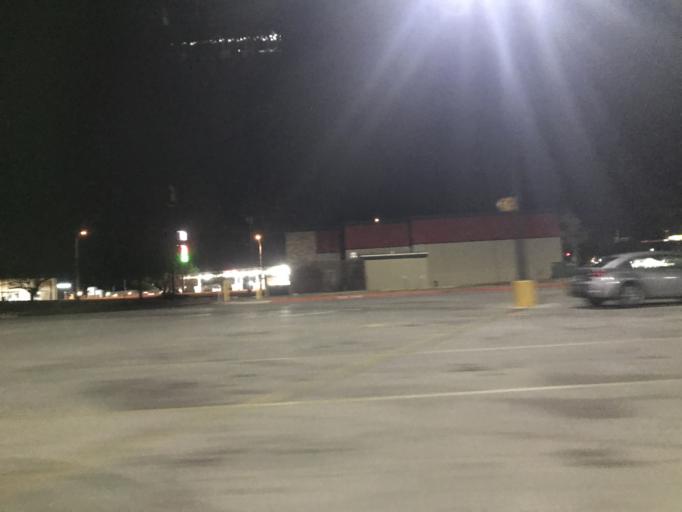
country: US
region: Texas
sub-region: Taylor County
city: Abilene
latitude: 32.4800
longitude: -99.6967
